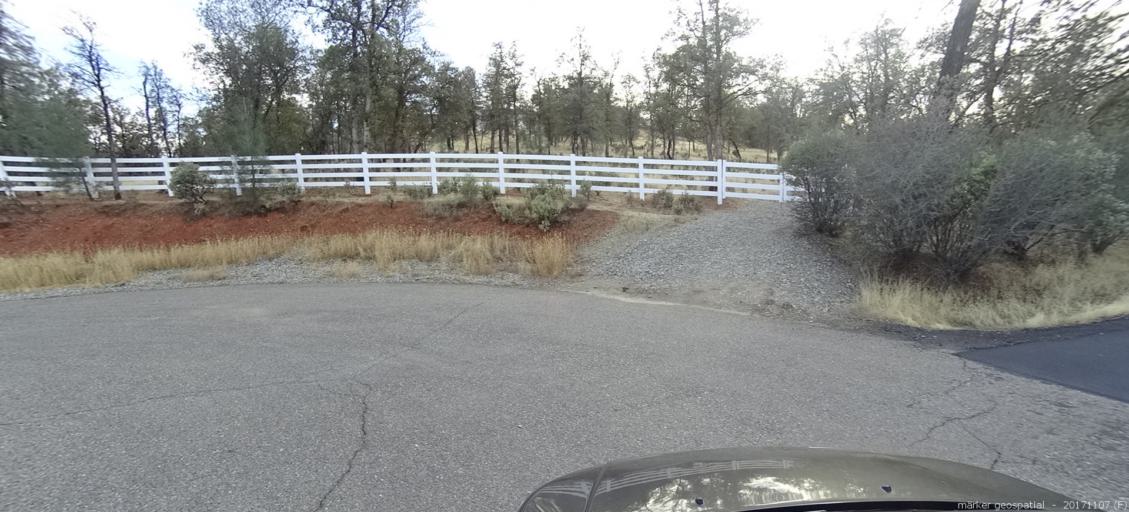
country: US
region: California
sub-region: Shasta County
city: Shasta
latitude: 40.5157
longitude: -122.4815
